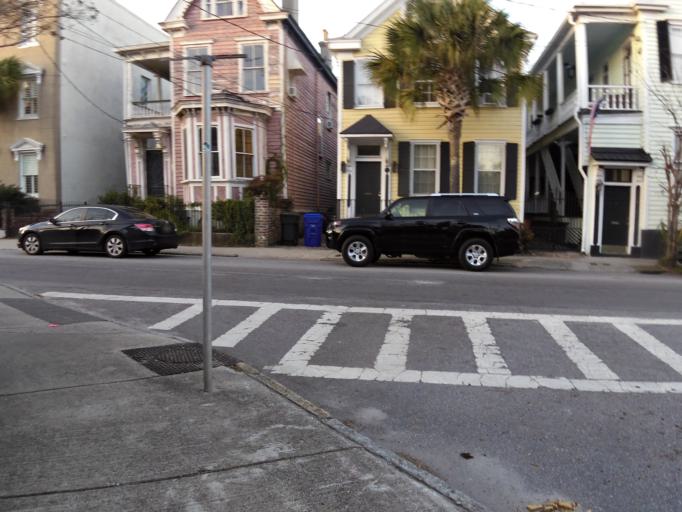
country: US
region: South Carolina
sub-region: Charleston County
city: Charleston
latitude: 32.7775
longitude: -79.9349
